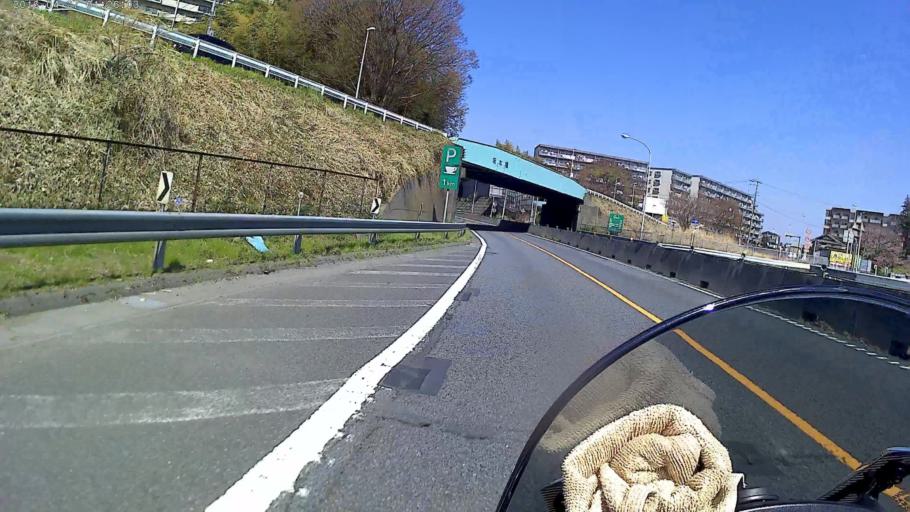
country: JP
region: Kanagawa
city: Fujisawa
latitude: 35.4132
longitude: 139.5337
